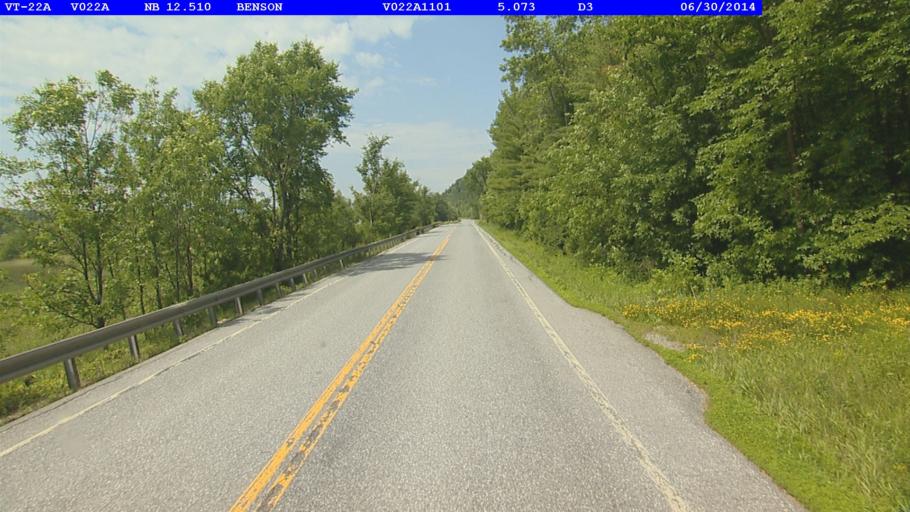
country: US
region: Vermont
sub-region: Rutland County
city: Fair Haven
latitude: 43.7406
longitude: -73.3068
